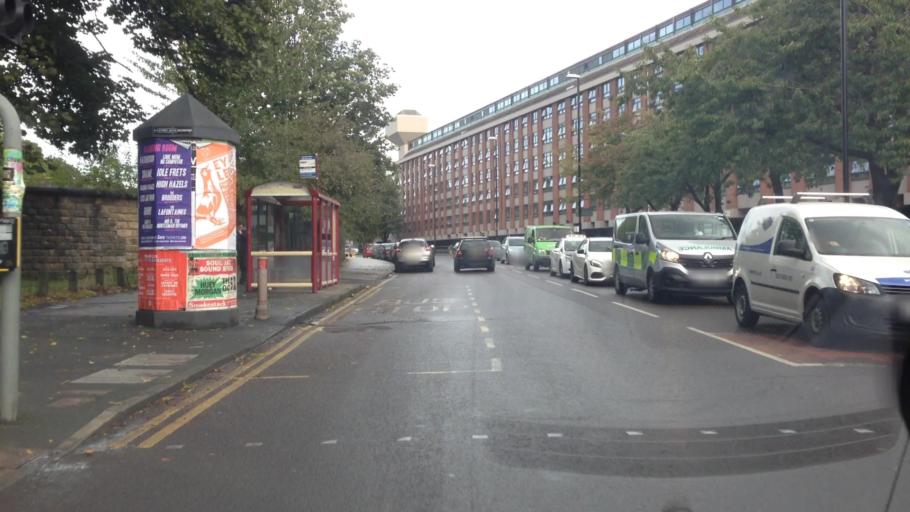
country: GB
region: England
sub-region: City and Borough of Leeds
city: Leeds
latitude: 53.8081
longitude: -1.5594
